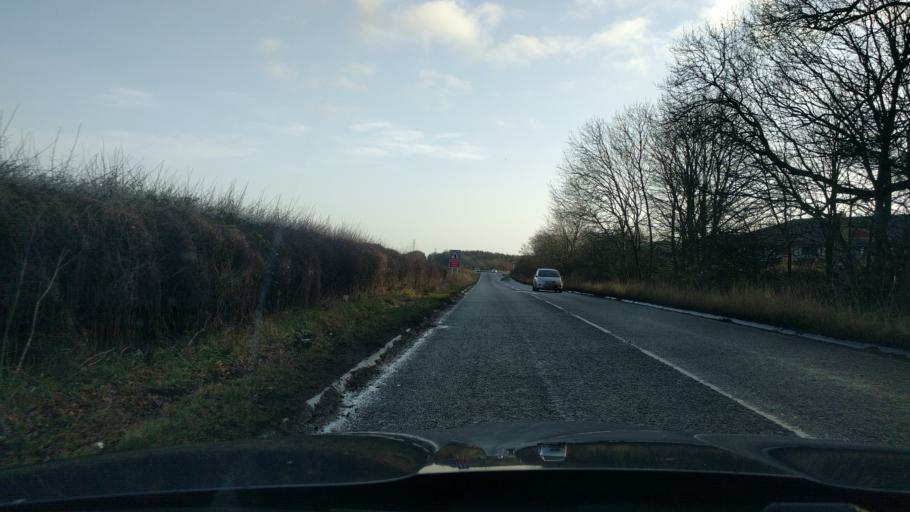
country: GB
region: England
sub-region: Northumberland
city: Cresswell
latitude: 55.1981
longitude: -1.5549
